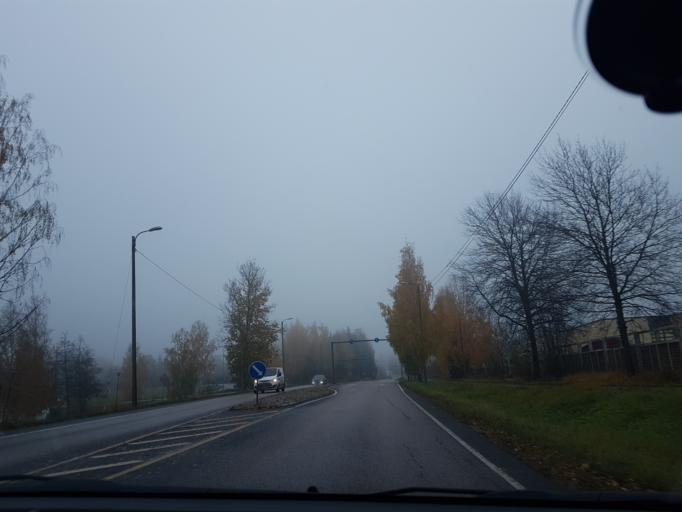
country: FI
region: Uusimaa
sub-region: Helsinki
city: Tuusula
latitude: 60.4097
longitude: 25.0407
